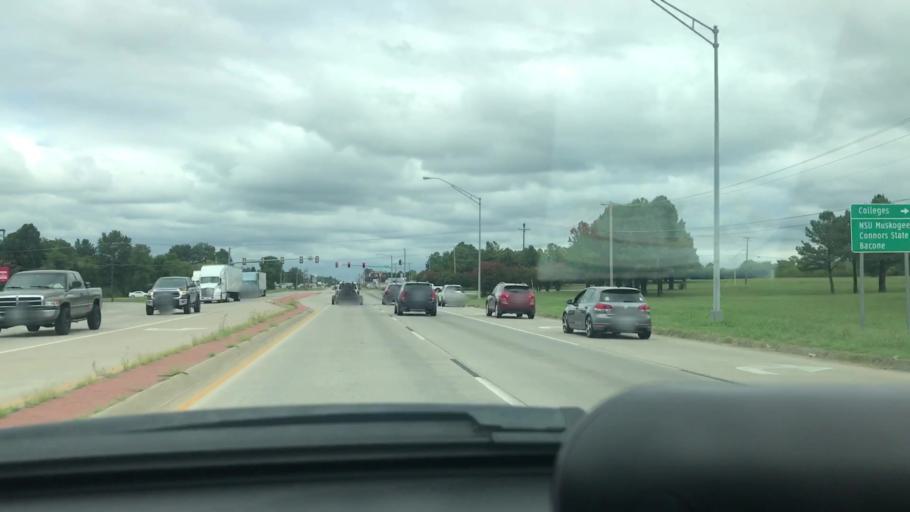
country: US
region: Oklahoma
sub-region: Muskogee County
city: Muskogee
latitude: 35.7677
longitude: -95.4024
